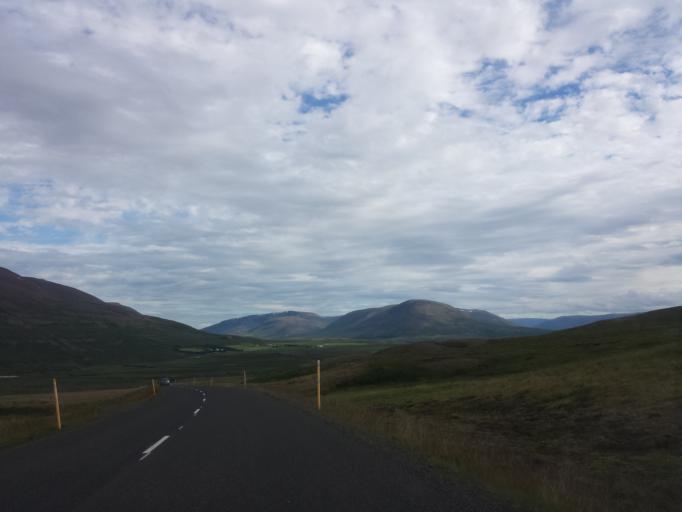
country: IS
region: Northeast
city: Akureyri
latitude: 65.7935
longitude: -17.9366
